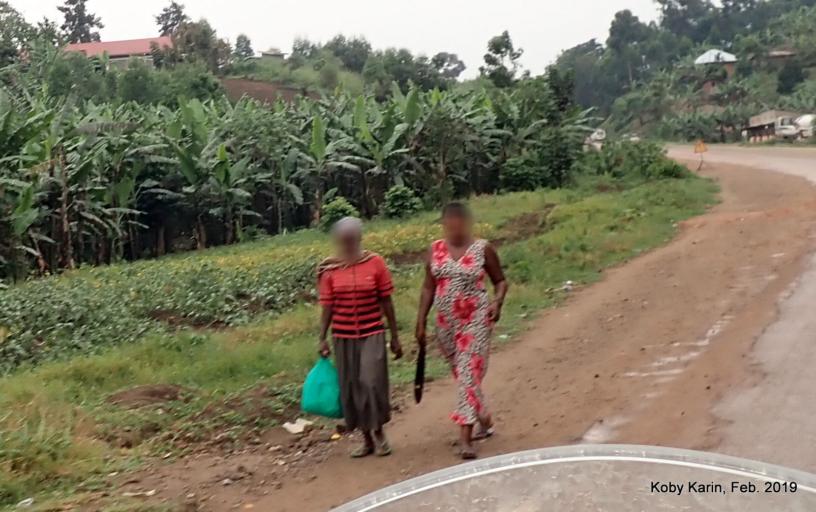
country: UG
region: Western Region
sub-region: Rubirizi District
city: Rubirizi
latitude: -0.2707
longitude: 30.1063
